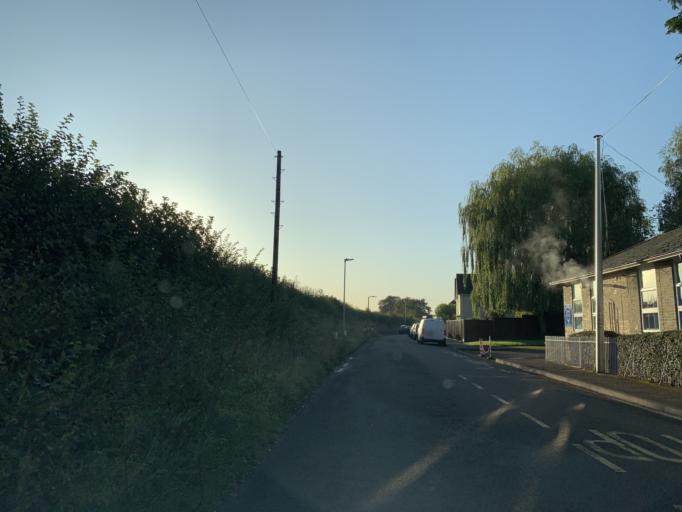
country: GB
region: England
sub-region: Wiltshire
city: Salisbury
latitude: 51.0912
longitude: -1.8140
